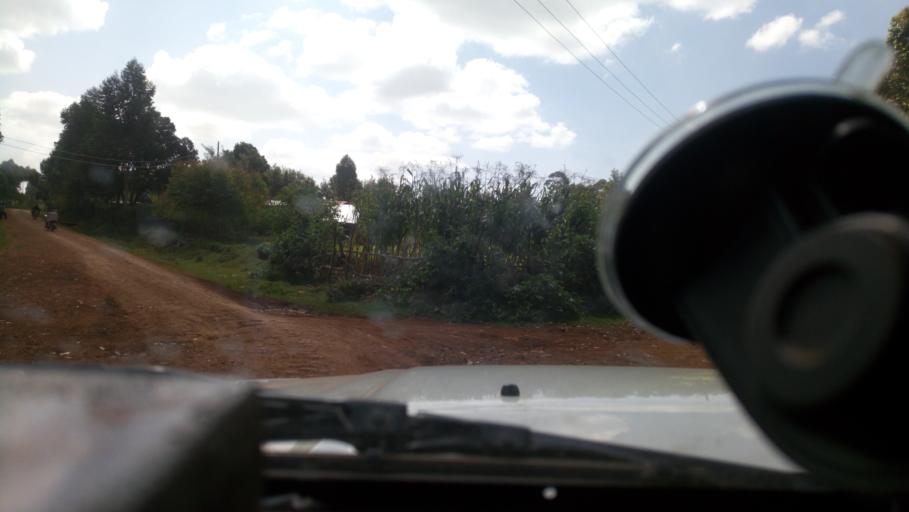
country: KE
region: Nyamira District
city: Nyamira
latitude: -0.6190
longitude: 34.9063
